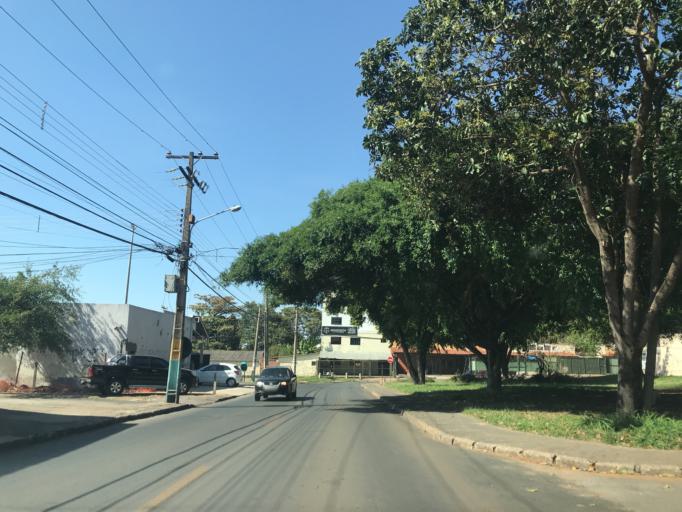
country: BR
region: Federal District
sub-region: Brasilia
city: Brasilia
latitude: -15.8170
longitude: -48.0803
